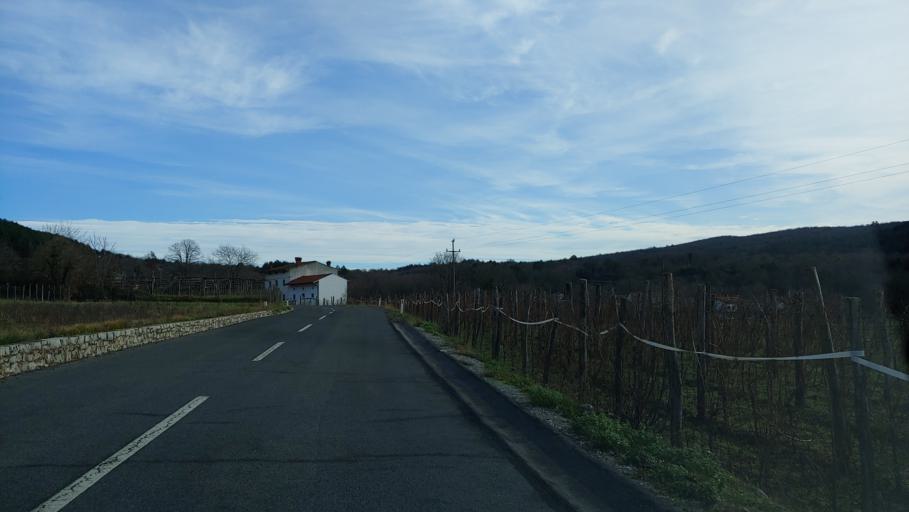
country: IT
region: Friuli Venezia Giulia
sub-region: Provincia di Trieste
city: Sistiana-Visogliano
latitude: 45.8126
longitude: 13.6384
